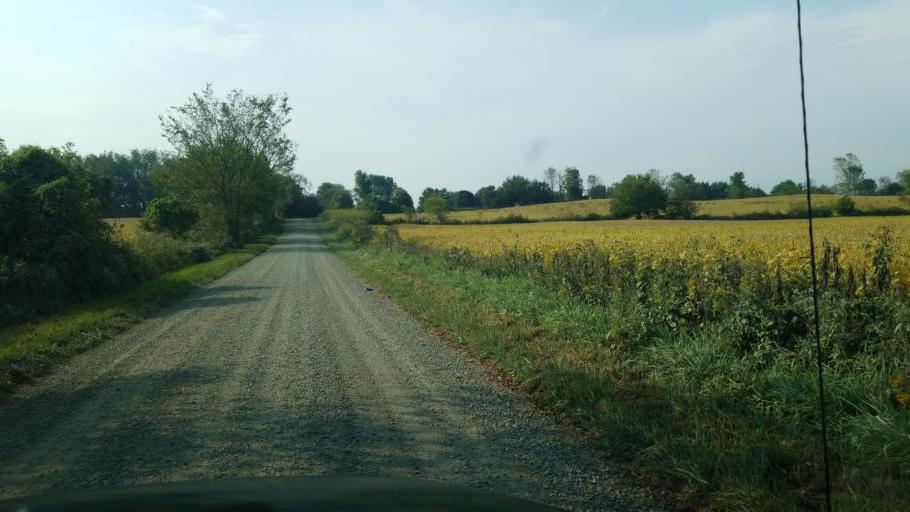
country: US
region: Ohio
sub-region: Knox County
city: Centerburg
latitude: 40.2725
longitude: -82.5854
